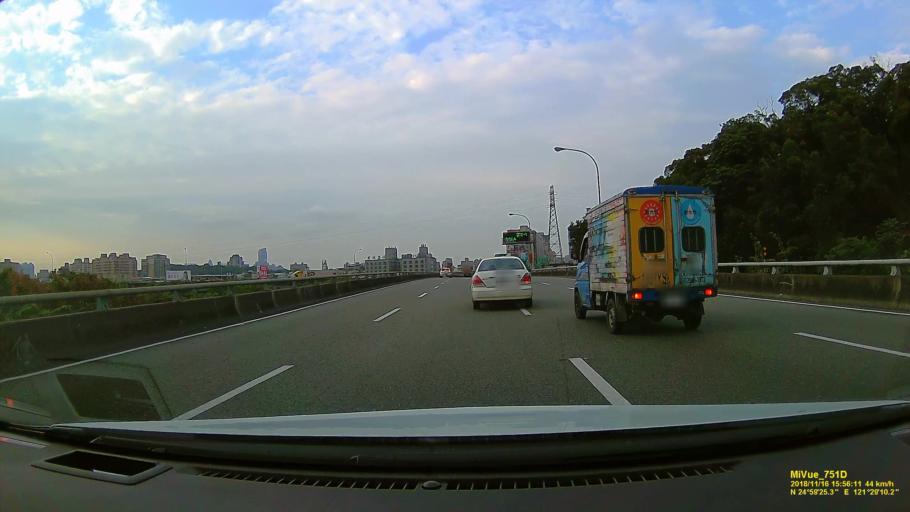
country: TW
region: Taipei
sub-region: Taipei
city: Banqiao
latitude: 24.9900
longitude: 121.4861
